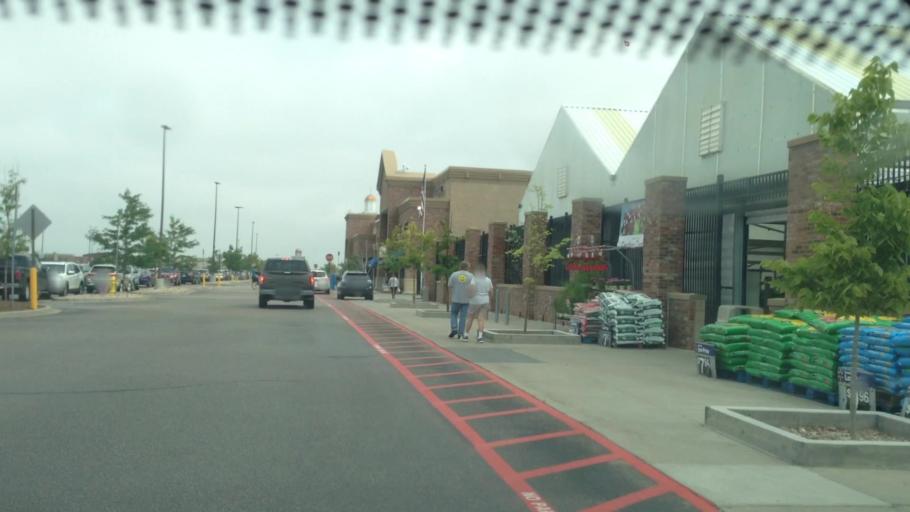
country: US
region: Colorado
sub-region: Douglas County
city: Parker
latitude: 39.6053
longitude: -104.7055
